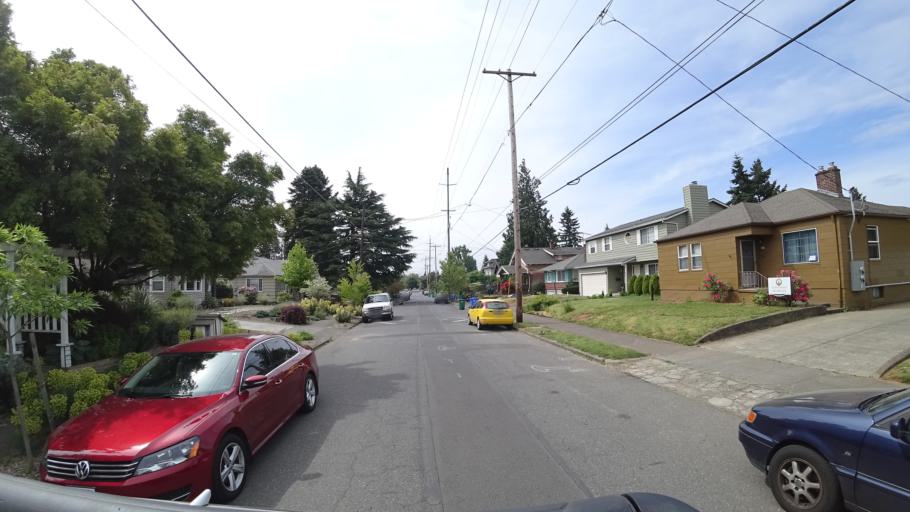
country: US
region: Oregon
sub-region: Multnomah County
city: Lents
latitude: 45.5299
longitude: -122.6088
